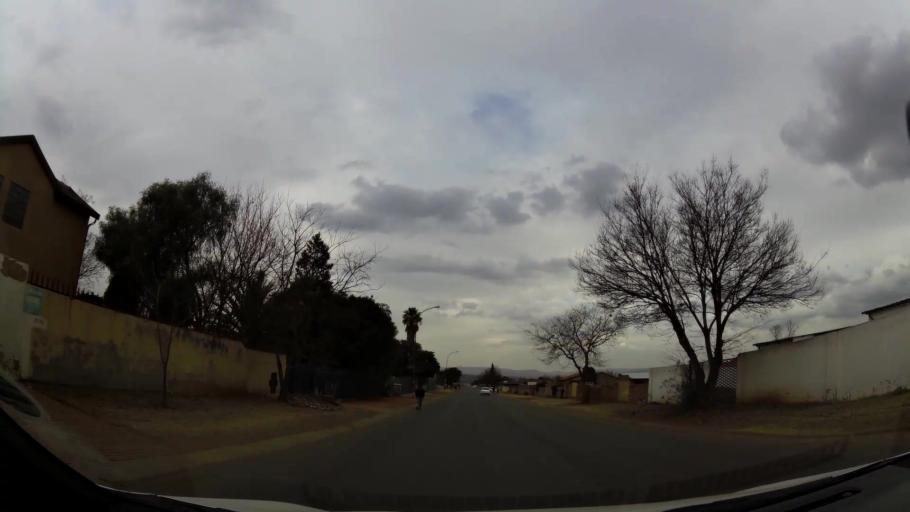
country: ZA
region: Gauteng
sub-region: Ekurhuleni Metropolitan Municipality
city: Germiston
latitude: -26.3919
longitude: 28.1506
